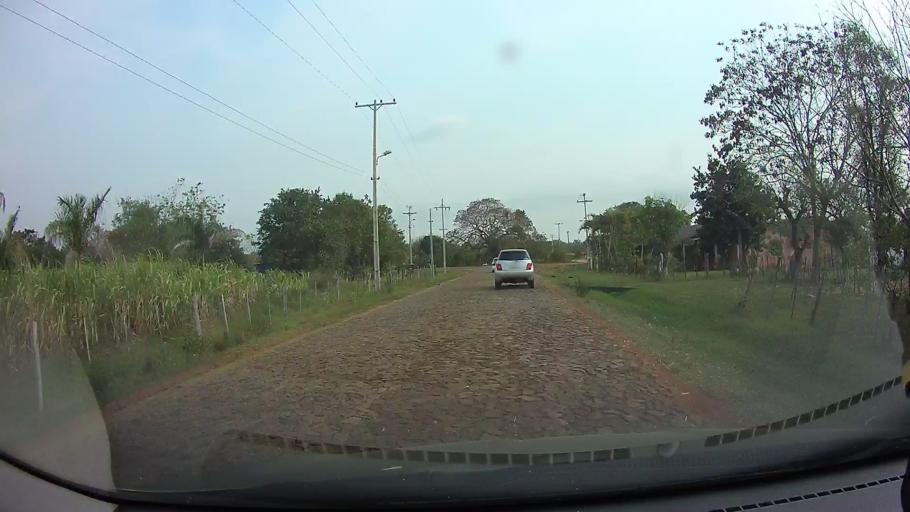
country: PY
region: Cordillera
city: Arroyos y Esteros
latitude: -25.0370
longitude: -57.1090
